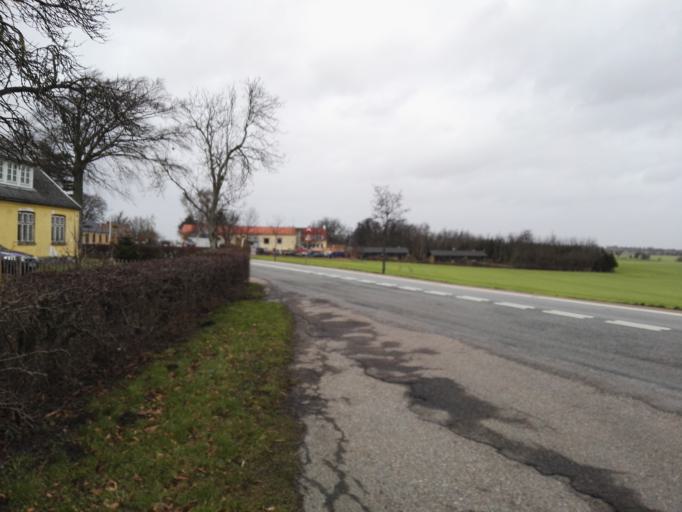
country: DK
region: Zealand
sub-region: Lejre Kommune
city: Ejby
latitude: 55.6832
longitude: 11.9205
